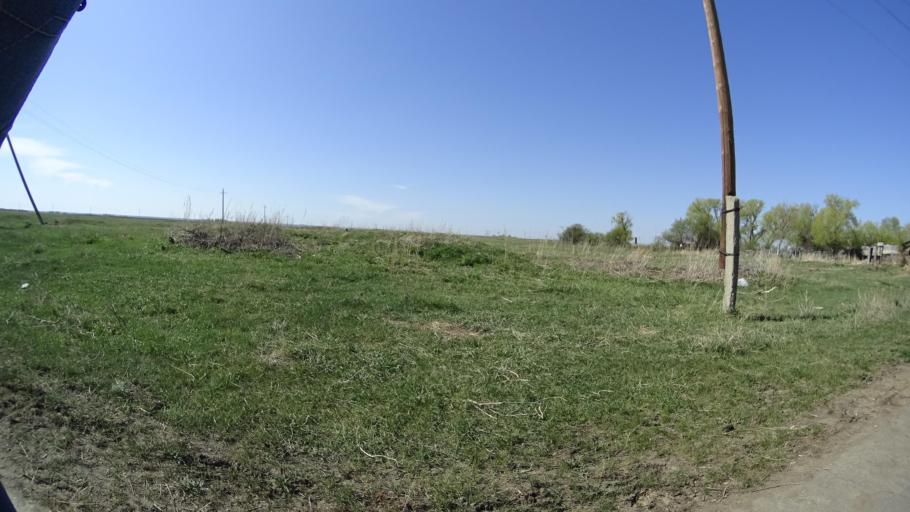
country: RU
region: Chelyabinsk
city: Chesma
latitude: 53.8001
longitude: 61.0172
